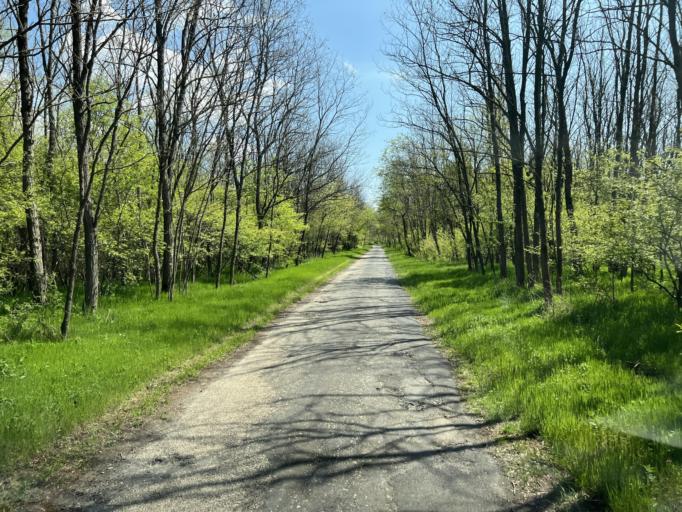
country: HU
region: Pest
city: Kakucs
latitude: 47.2712
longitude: 19.3603
